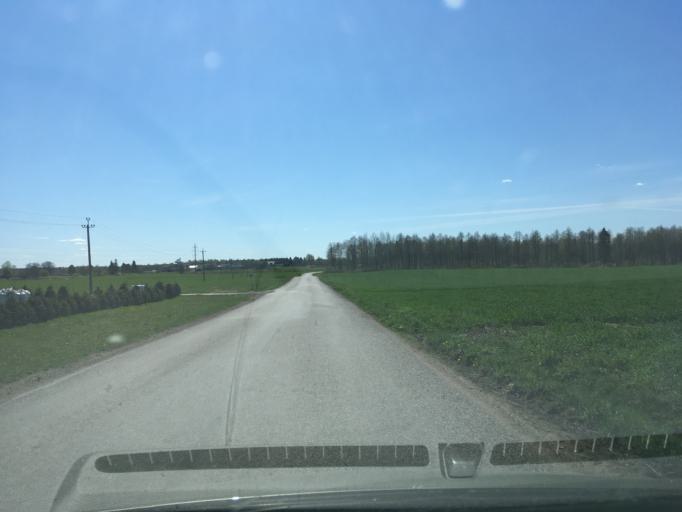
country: EE
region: Harju
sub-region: Raasiku vald
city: Arukula
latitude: 59.3888
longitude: 25.0803
